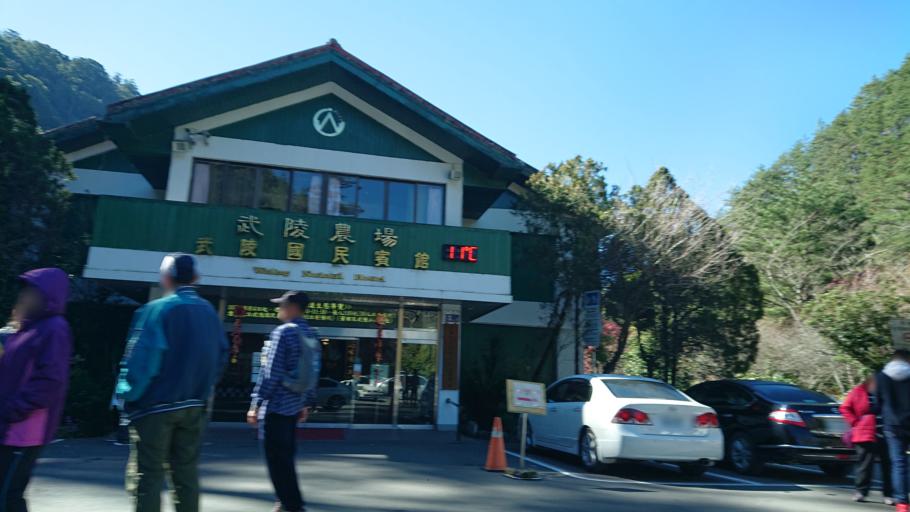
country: TW
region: Taiwan
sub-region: Hualien
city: Hualian
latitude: 24.3466
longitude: 121.3083
